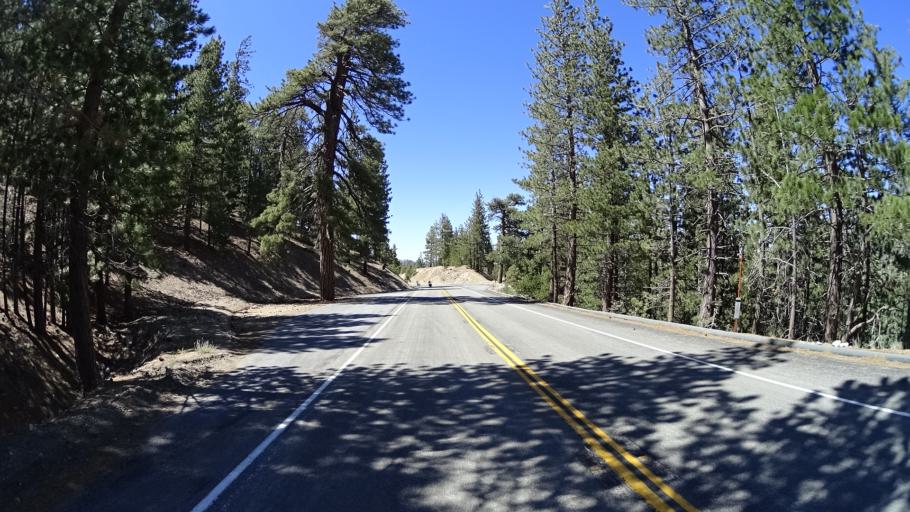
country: US
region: California
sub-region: San Bernardino County
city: Wrightwood
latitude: 34.3526
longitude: -117.8353
